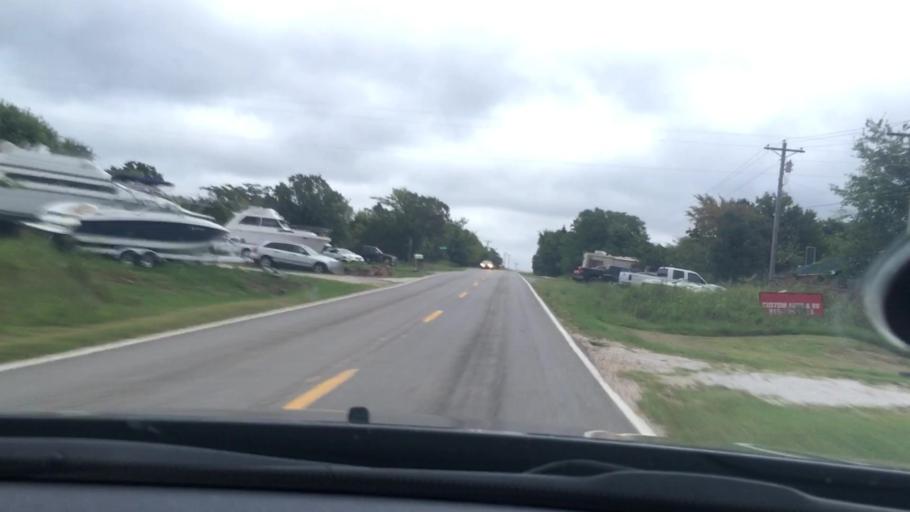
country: US
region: Oklahoma
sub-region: Sequoyah County
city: Vian
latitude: 35.6024
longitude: -95.0174
